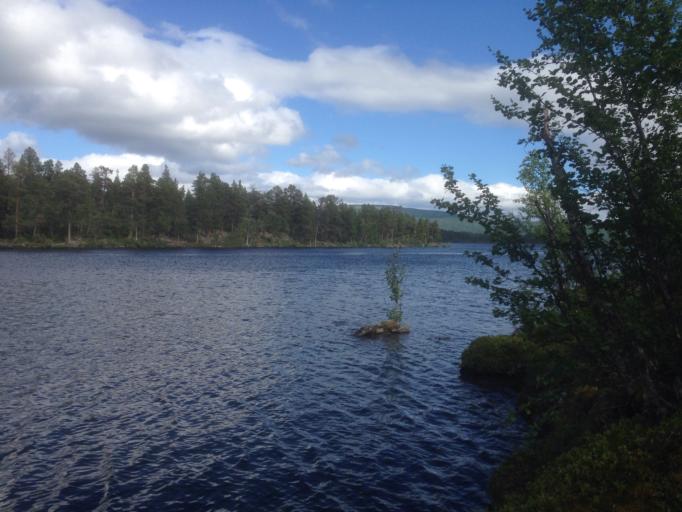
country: SE
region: Norrbotten
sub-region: Arjeplogs Kommun
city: Arjeplog
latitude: 66.4241
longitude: 16.9401
